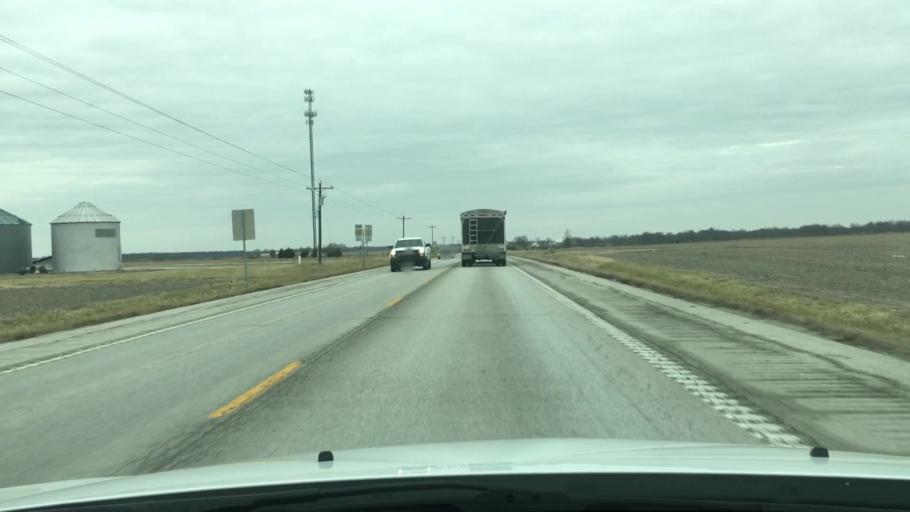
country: US
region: Missouri
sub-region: Montgomery County
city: Wellsville
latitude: 39.1669
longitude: -91.6478
